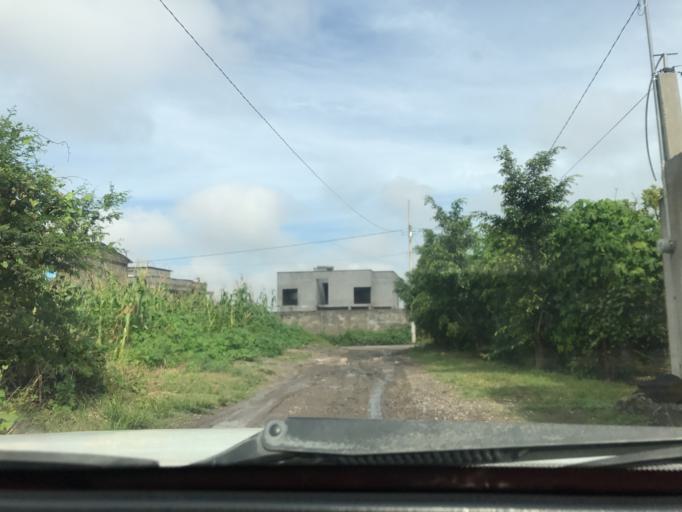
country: MX
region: Morelos
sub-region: Yecapixtla
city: Mixtlalcingo
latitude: 18.7994
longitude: -98.9103
